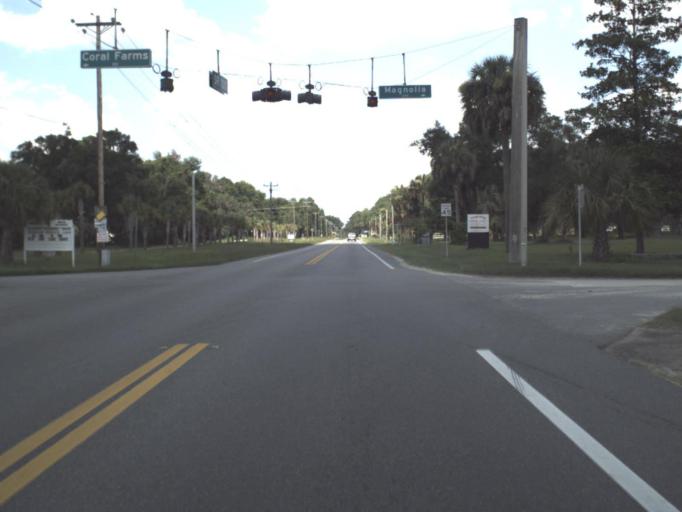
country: US
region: Florida
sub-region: Putnam County
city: Interlachen
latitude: 29.7325
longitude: -81.8880
